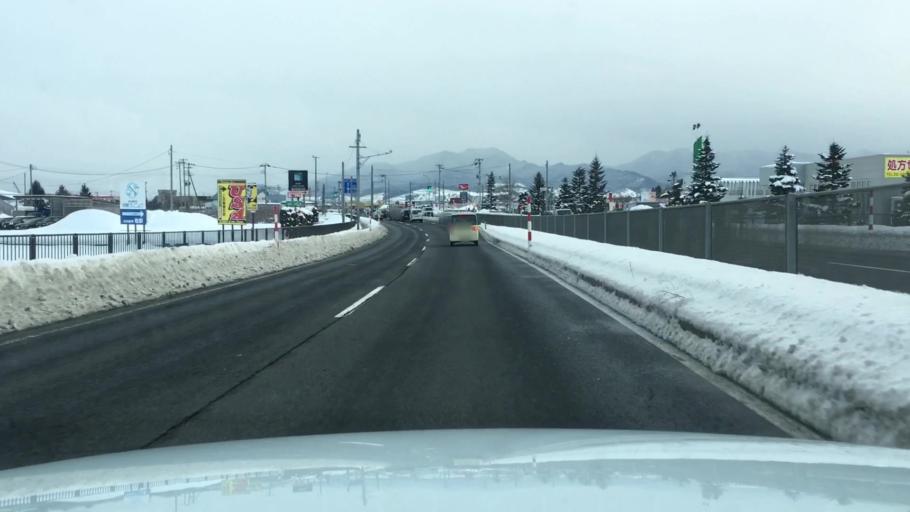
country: JP
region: Aomori
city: Hirosaki
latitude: 40.5873
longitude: 140.5070
